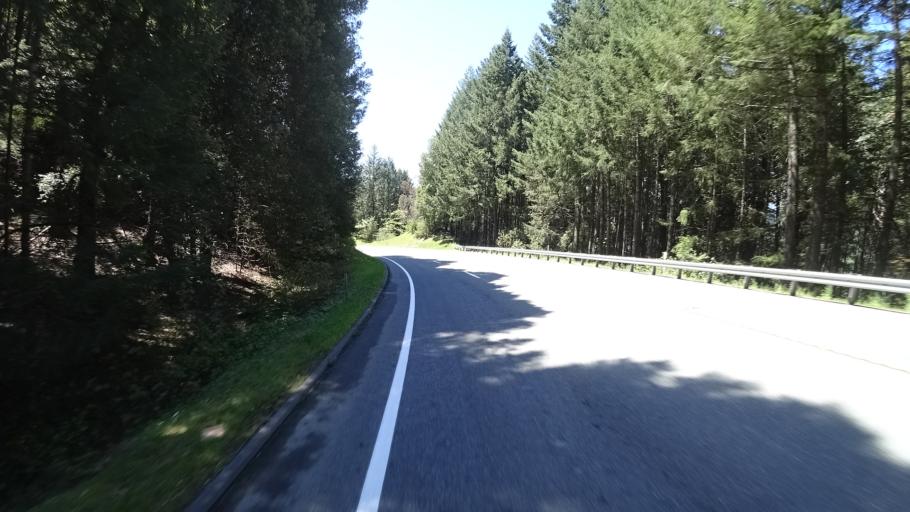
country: US
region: California
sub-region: Humboldt County
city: Willow Creek
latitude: 40.9150
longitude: -123.8040
